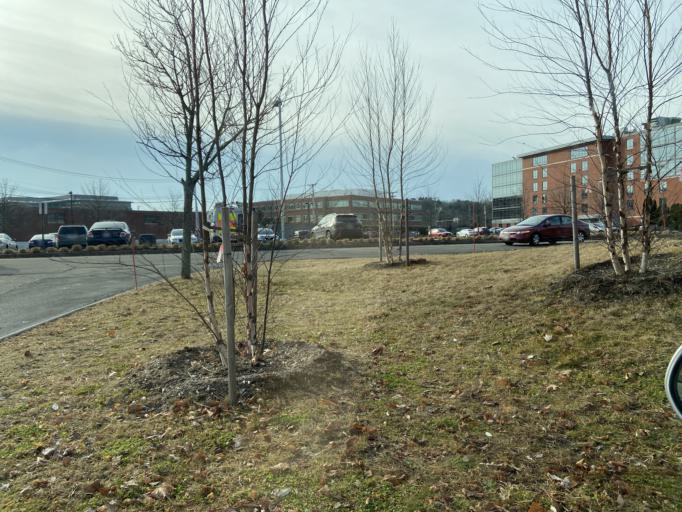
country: US
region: Massachusetts
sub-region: Norfolk County
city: Needham
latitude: 42.3013
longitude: -71.2204
